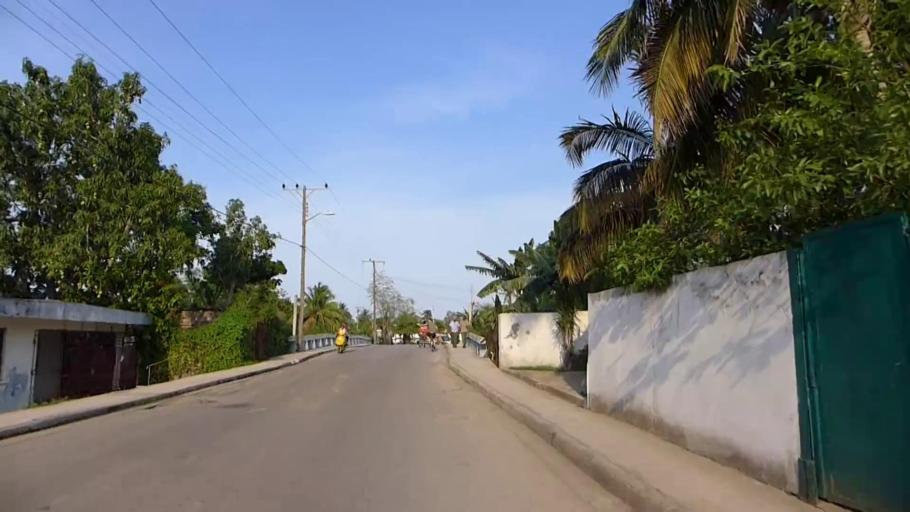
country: CU
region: Camaguey
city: Camaguey
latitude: 21.3840
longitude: -77.9060
